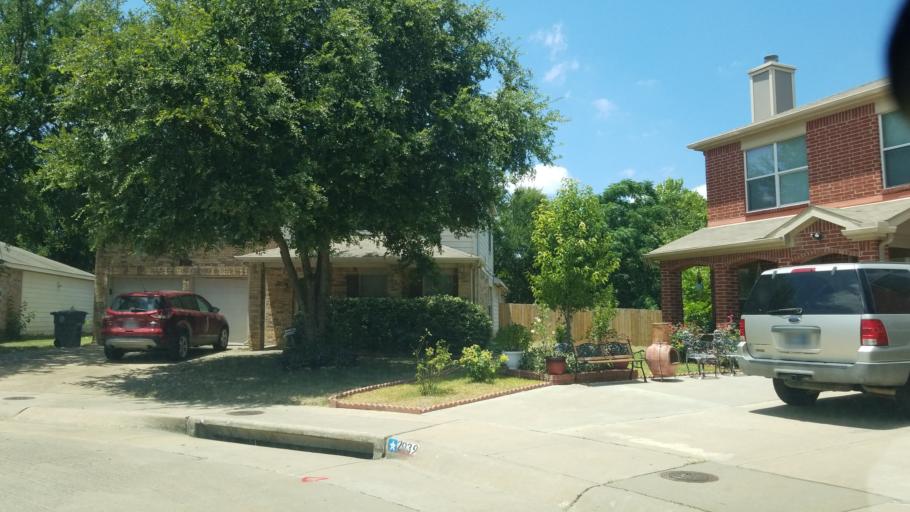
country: US
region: Texas
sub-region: Dallas County
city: Balch Springs
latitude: 32.7478
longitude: -96.7008
